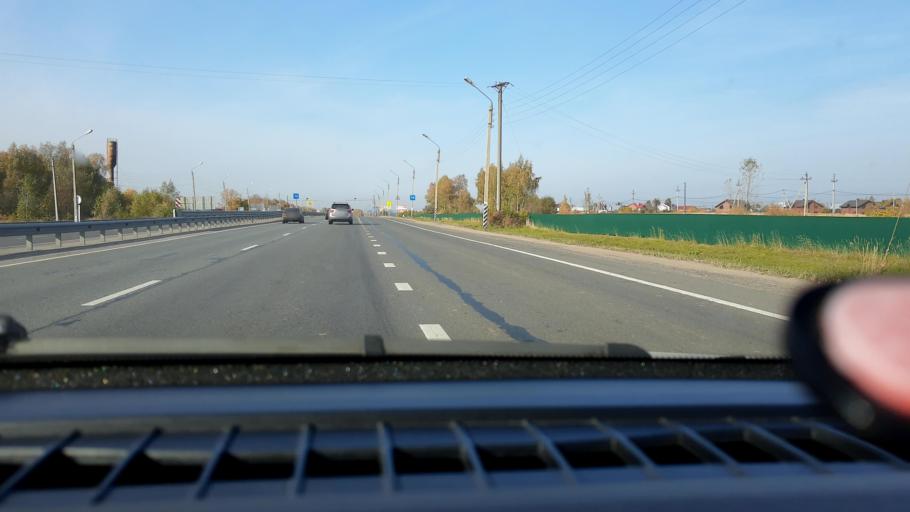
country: RU
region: Nizjnij Novgorod
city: Kstovo
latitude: 56.1282
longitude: 44.2590
